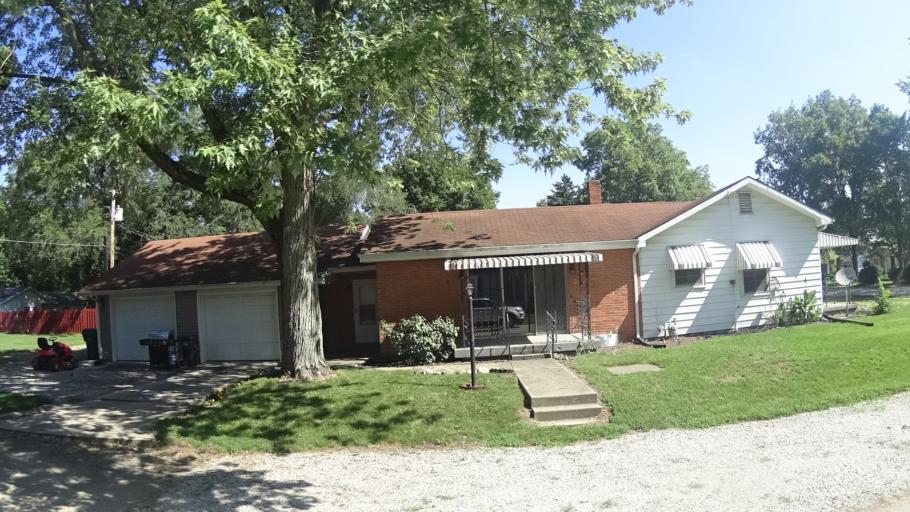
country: US
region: Indiana
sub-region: Madison County
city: Pendleton
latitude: 39.9929
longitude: -85.7448
